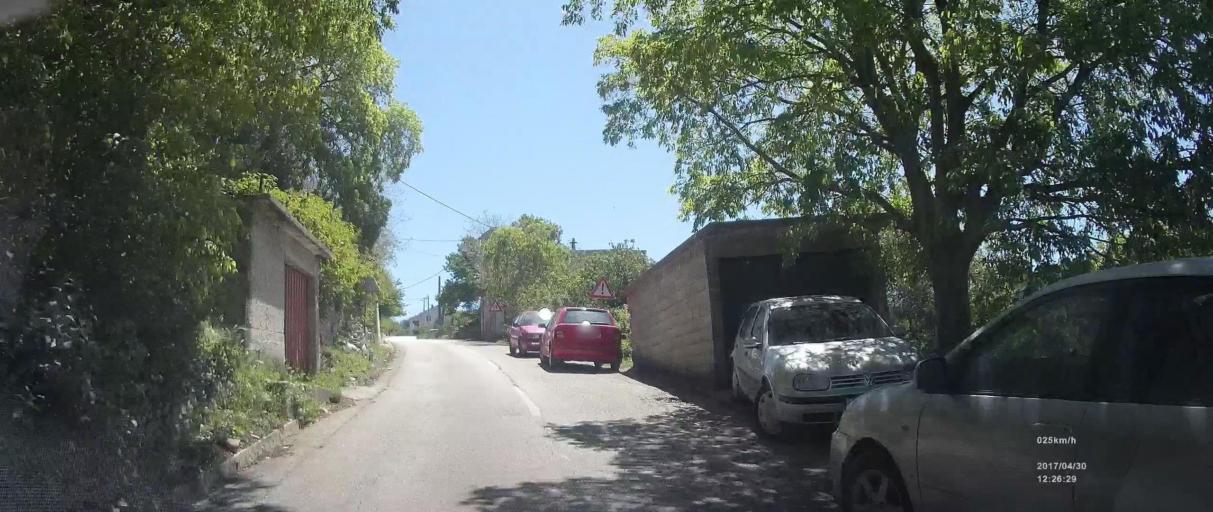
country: HR
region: Splitsko-Dalmatinska
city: Srinjine
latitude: 43.5086
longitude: 16.5940
